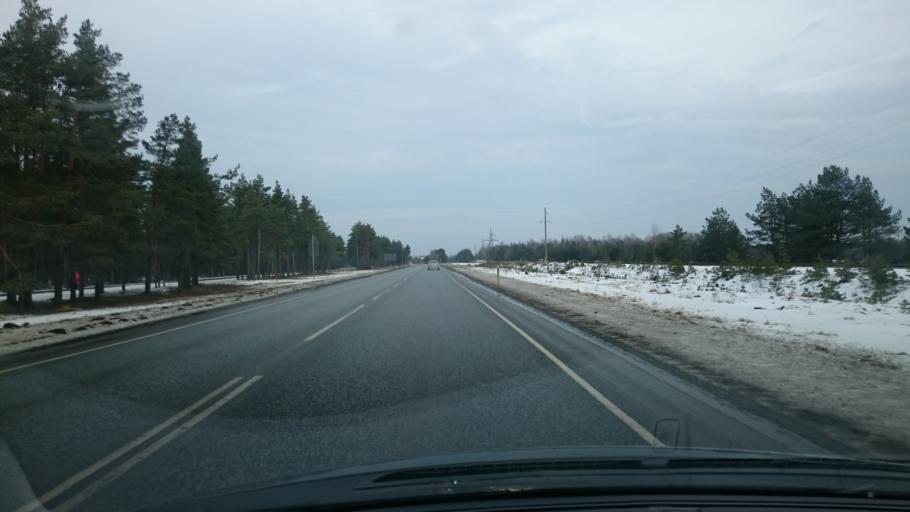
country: EE
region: Harju
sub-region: Saku vald
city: Saku
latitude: 59.3577
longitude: 24.7139
